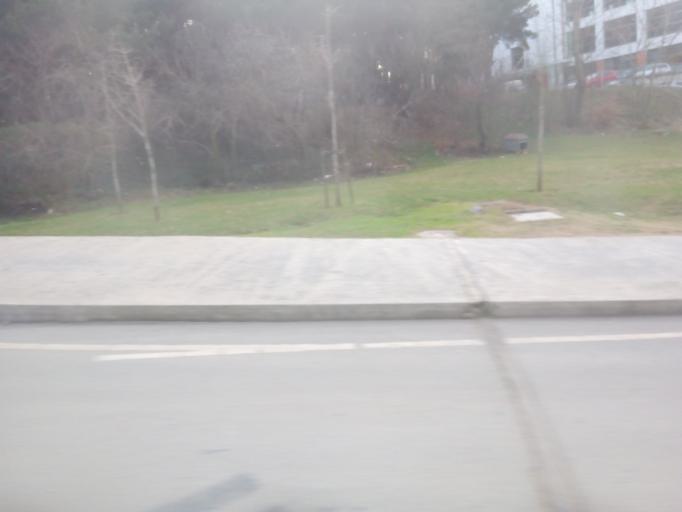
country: TR
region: Istanbul
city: Sisli
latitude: 41.1090
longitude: 29.0330
